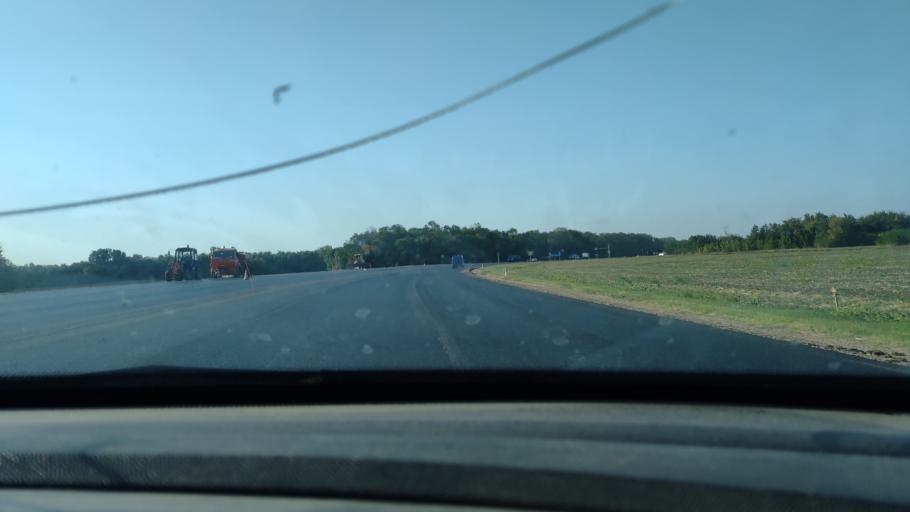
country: RU
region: Krasnodarskiy
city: Medvedovskaya
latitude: 45.5015
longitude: 38.9438
